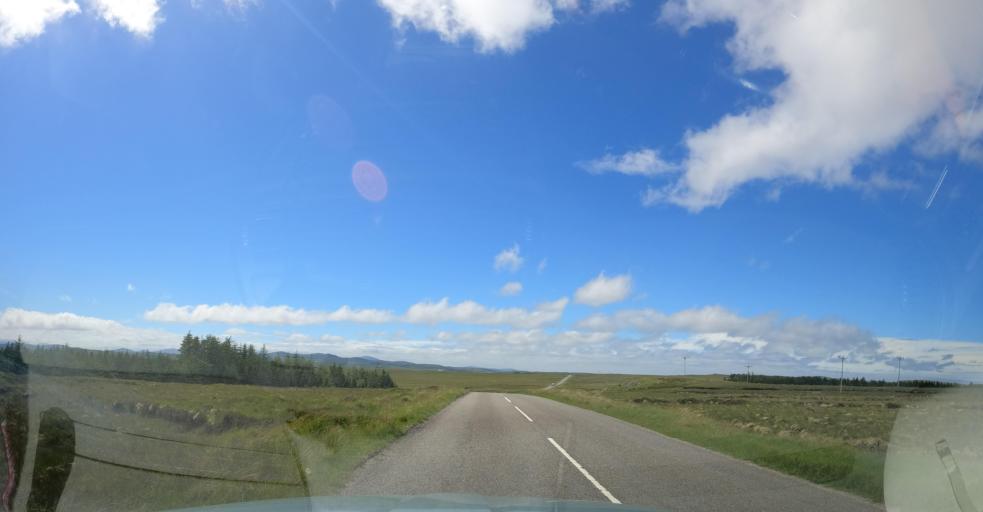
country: GB
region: Scotland
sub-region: Eilean Siar
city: Isle of Lewis
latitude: 58.1809
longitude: -6.6576
